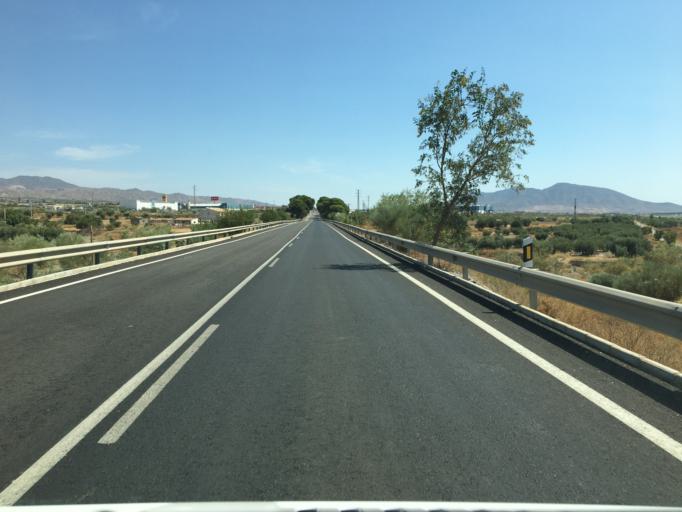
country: ES
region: Andalusia
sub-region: Provincia de Almeria
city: Huercal-Overa
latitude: 37.4278
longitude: -1.9151
